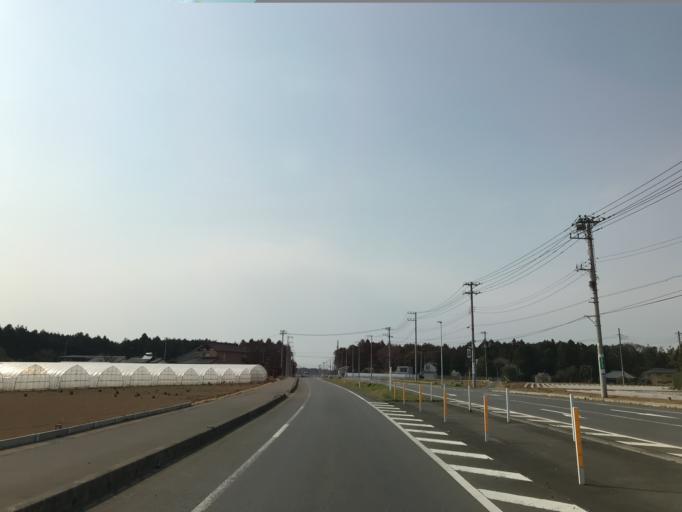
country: JP
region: Ibaraki
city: Okunoya
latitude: 36.1819
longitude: 140.4008
